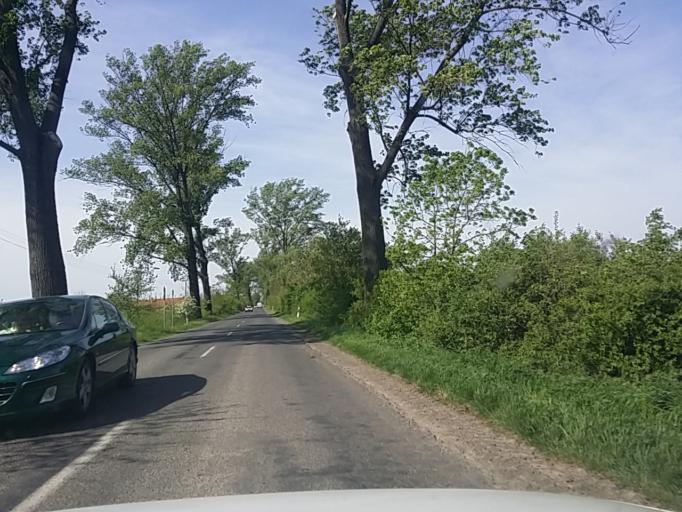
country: HU
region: Bekes
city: Doboz
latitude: 46.7139
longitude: 21.1856
